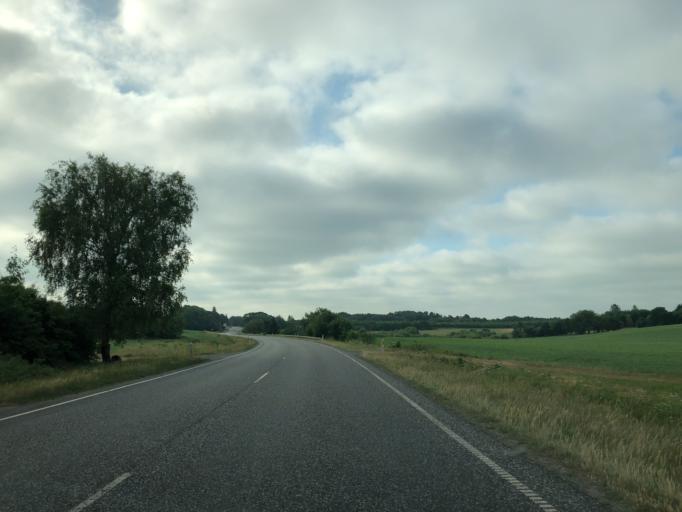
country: DK
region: South Denmark
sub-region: Vejle Kommune
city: Jelling
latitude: 55.7488
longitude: 9.3220
